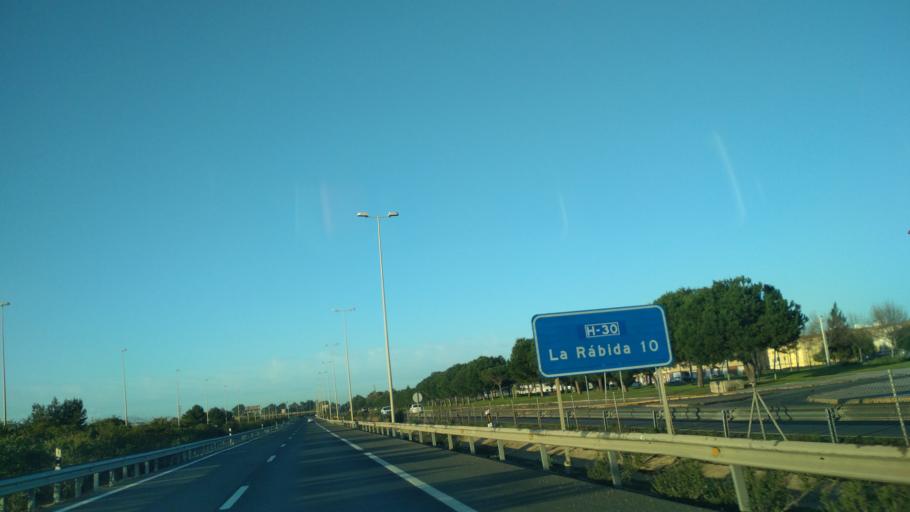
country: ES
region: Andalusia
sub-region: Provincia de Huelva
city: Huelva
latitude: 37.2575
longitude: -6.9231
